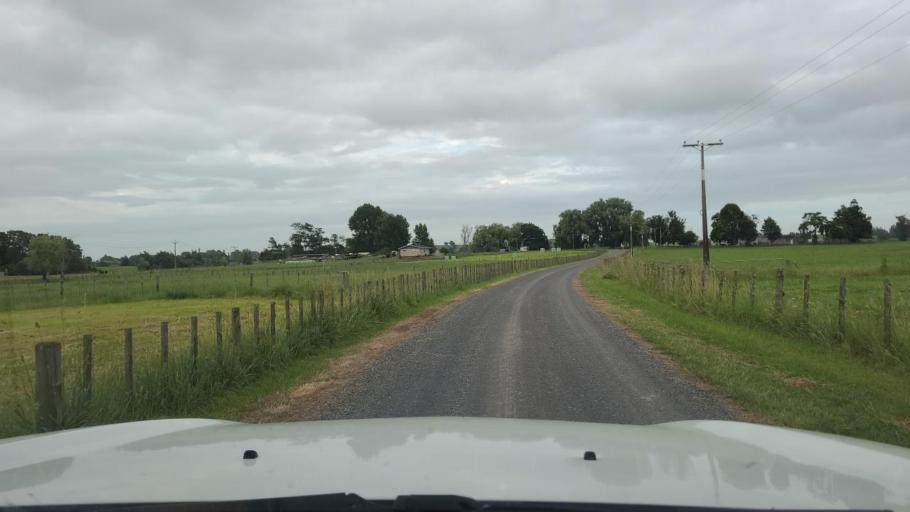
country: NZ
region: Waikato
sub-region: Hauraki District
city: Paeroa
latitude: -37.5722
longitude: 175.6669
